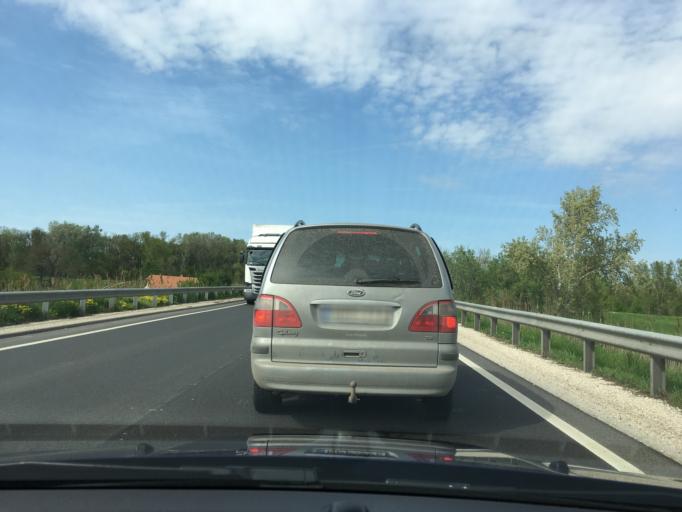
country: HU
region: Csongrad
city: Algyo
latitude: 46.3473
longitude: 20.2059
